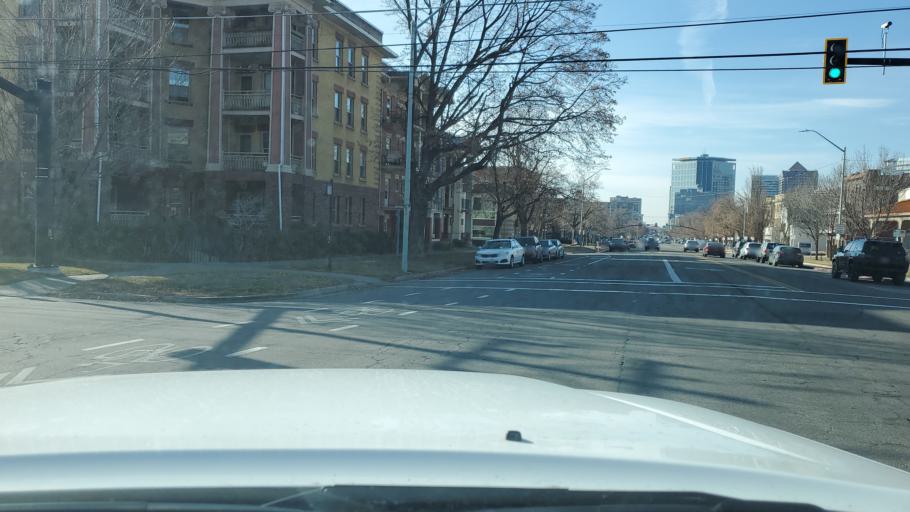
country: US
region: Utah
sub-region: Salt Lake County
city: Salt Lake City
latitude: 40.7628
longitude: -111.8768
